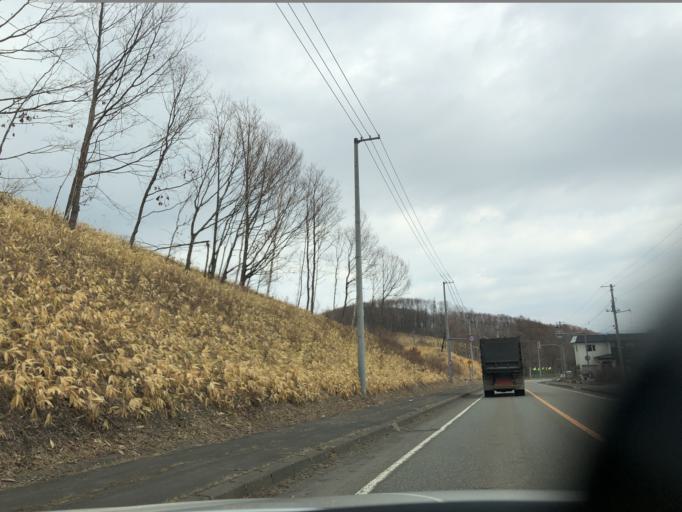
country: JP
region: Hokkaido
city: Chitose
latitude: 42.7621
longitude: 141.8026
